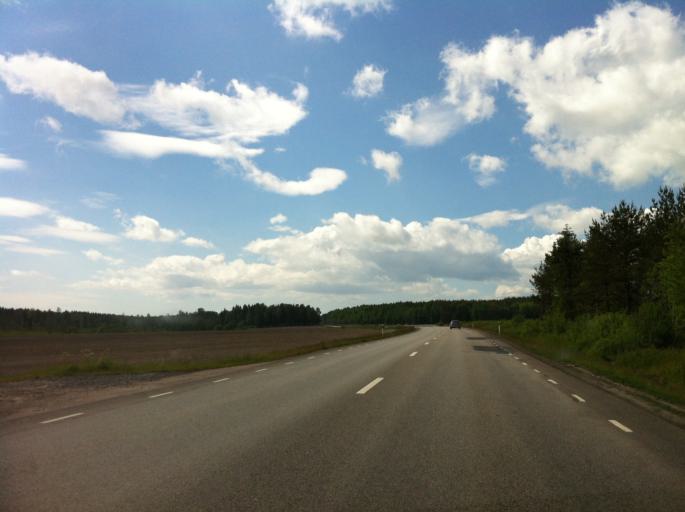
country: SE
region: Vaermland
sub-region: Saffle Kommun
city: Saeffle
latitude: 59.1784
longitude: 13.0088
